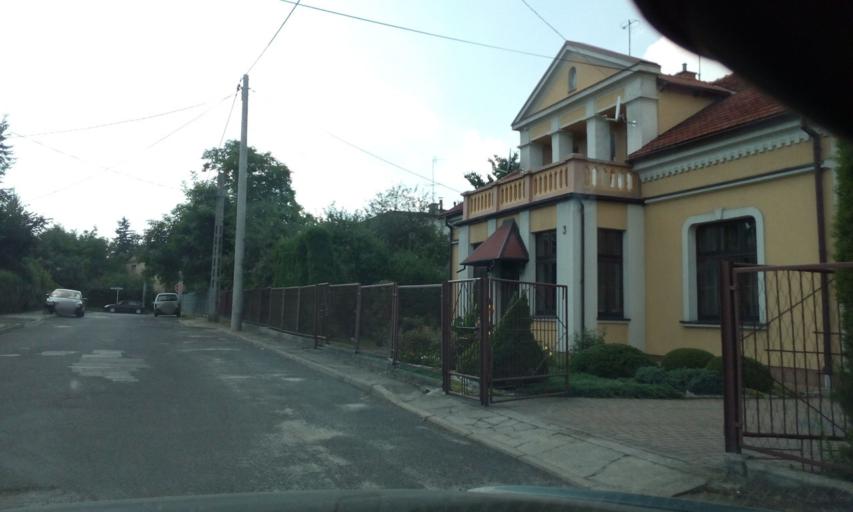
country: PL
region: Subcarpathian Voivodeship
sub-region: Powiat lancucki
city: Lancut
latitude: 50.0622
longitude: 22.2306
